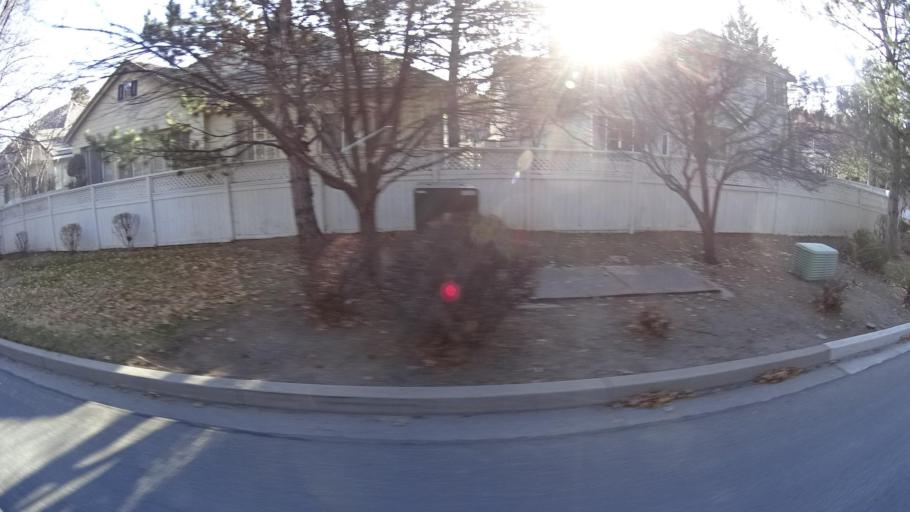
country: US
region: Nevada
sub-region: Washoe County
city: Reno
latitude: 39.4986
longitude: -119.8622
